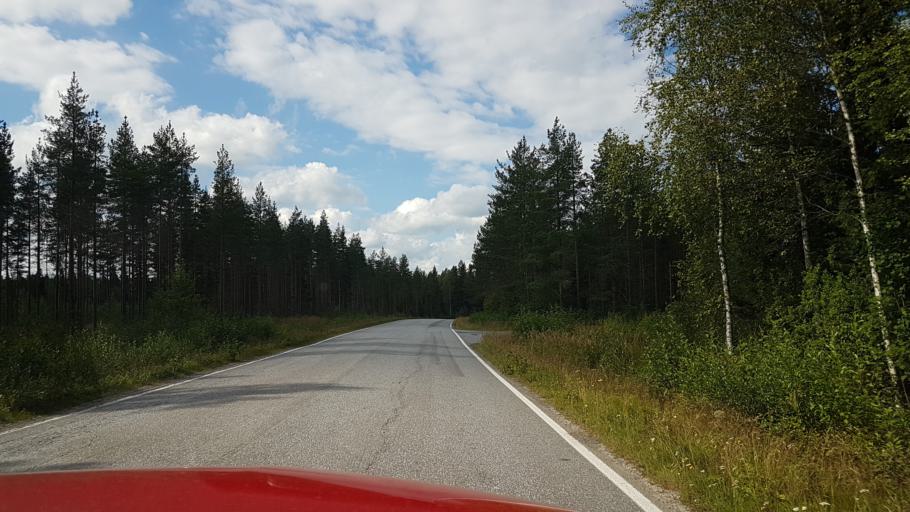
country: FI
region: Northern Ostrobothnia
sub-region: Ylivieska
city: Himanka
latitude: 64.0773
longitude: 23.7146
